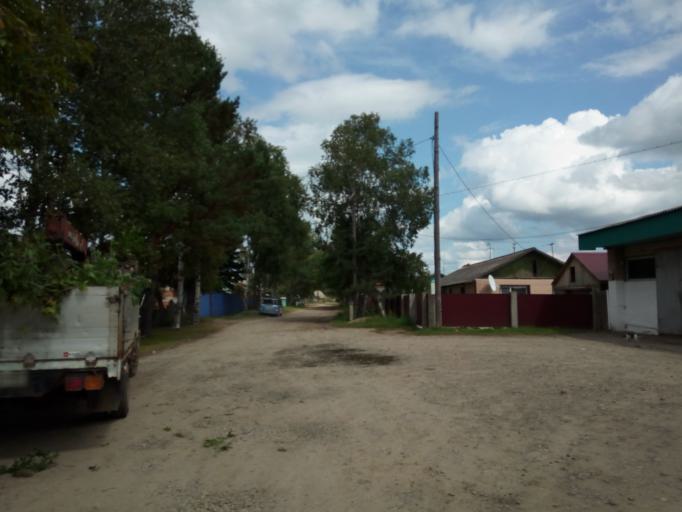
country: RU
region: Primorskiy
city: Dal'nerechensk
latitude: 45.9518
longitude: 133.8083
